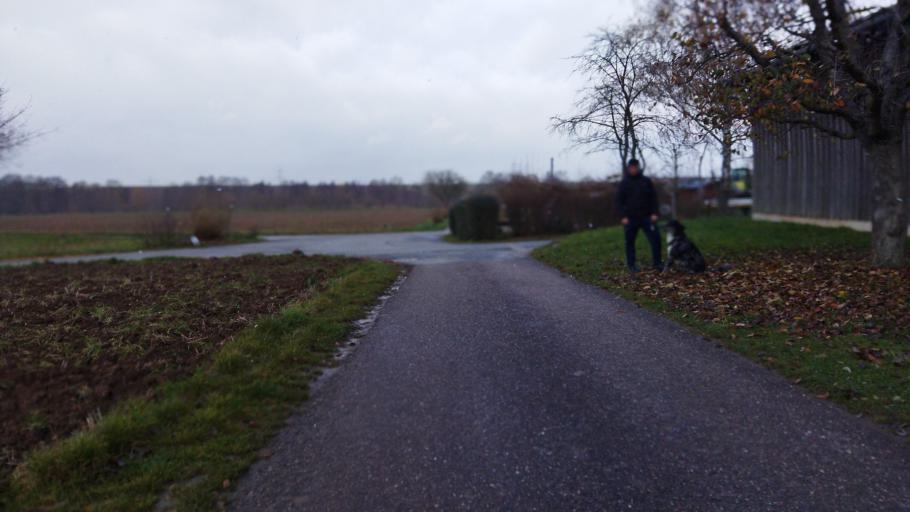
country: DE
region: Baden-Wuerttemberg
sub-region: Regierungsbezirk Stuttgart
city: Erligheim
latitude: 49.0221
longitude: 9.0888
